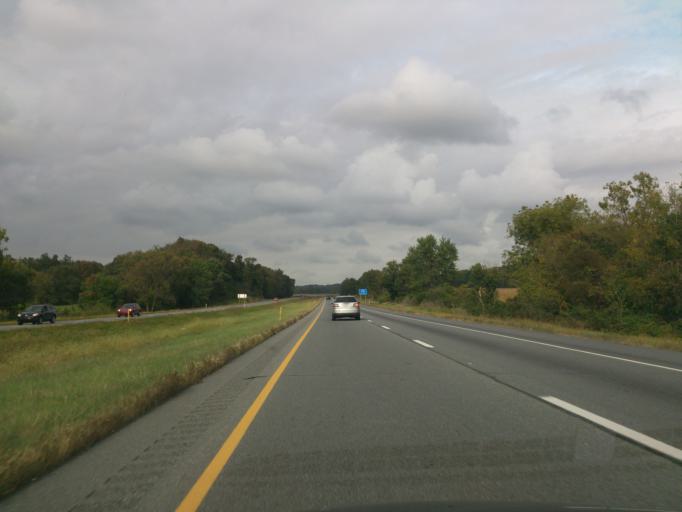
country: US
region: Pennsylvania
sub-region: Lancaster County
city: Adamstown
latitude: 40.2338
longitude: -76.0477
